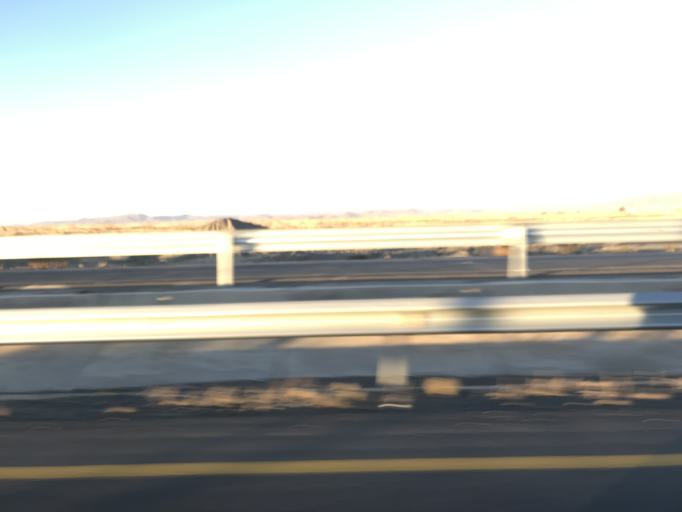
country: BO
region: La Paz
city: Batallas
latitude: -16.3116
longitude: -68.4532
